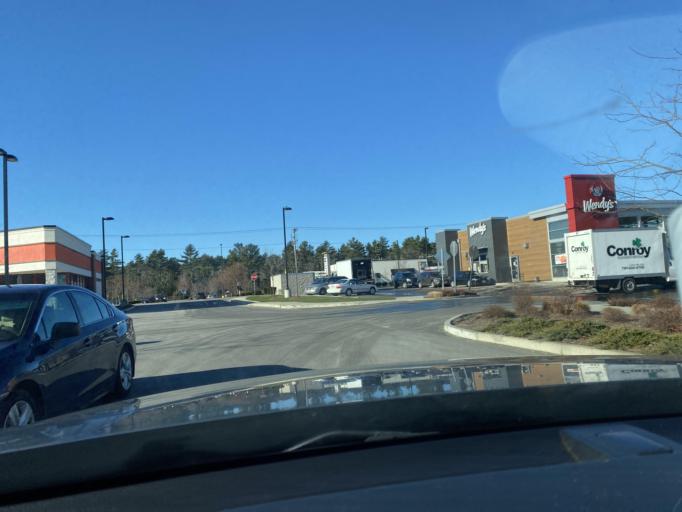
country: US
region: Massachusetts
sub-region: Plymouth County
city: West Wareham
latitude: 41.7801
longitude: -70.7438
